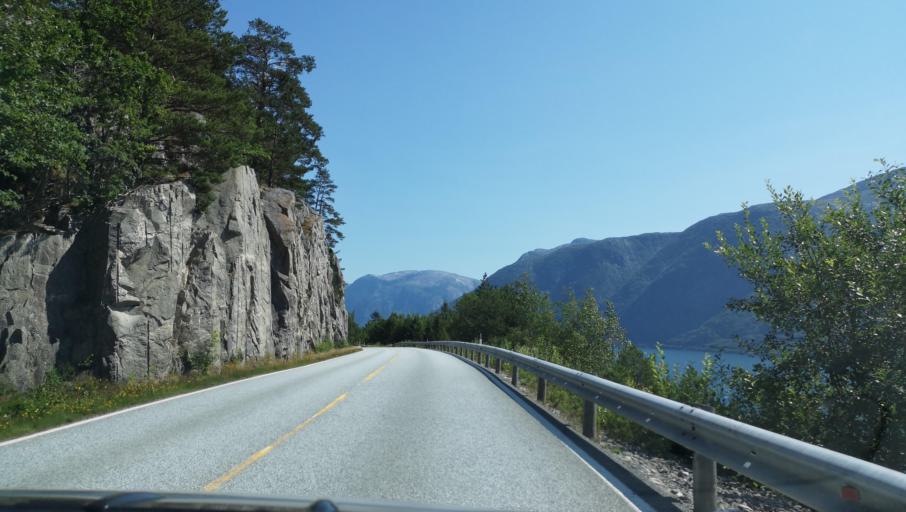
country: NO
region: Hordaland
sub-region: Ulvik
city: Ulvik
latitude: 60.4858
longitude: 6.8768
